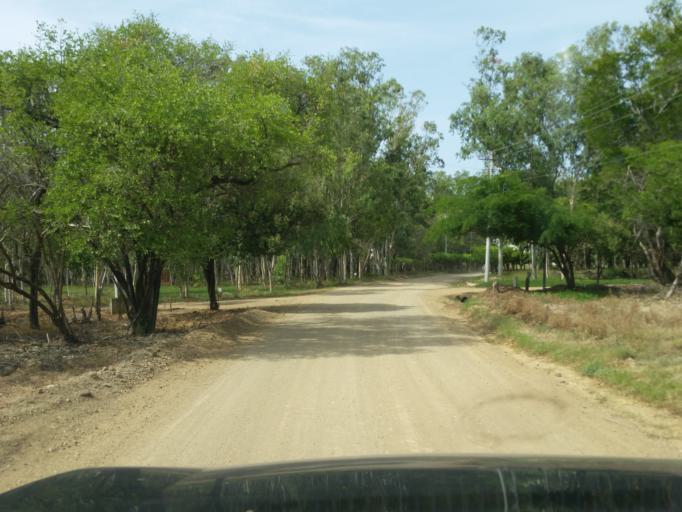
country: NI
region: Rivas
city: Tola
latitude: 11.4125
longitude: -86.0536
